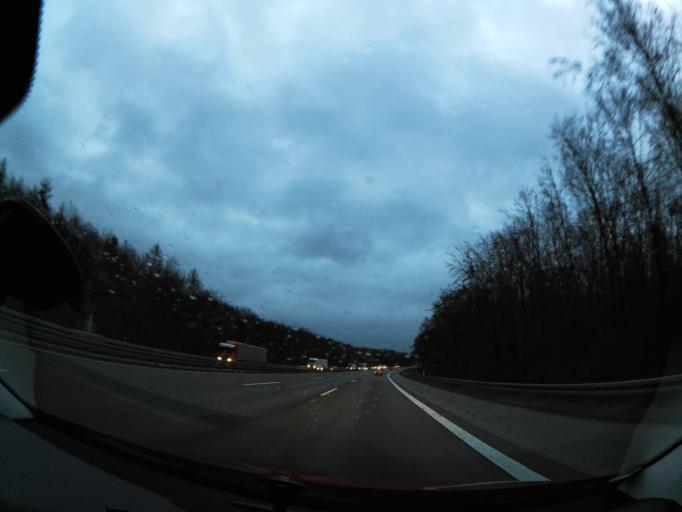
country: DE
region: Rheinland-Pfalz
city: Hambach
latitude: 50.4119
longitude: 7.9905
